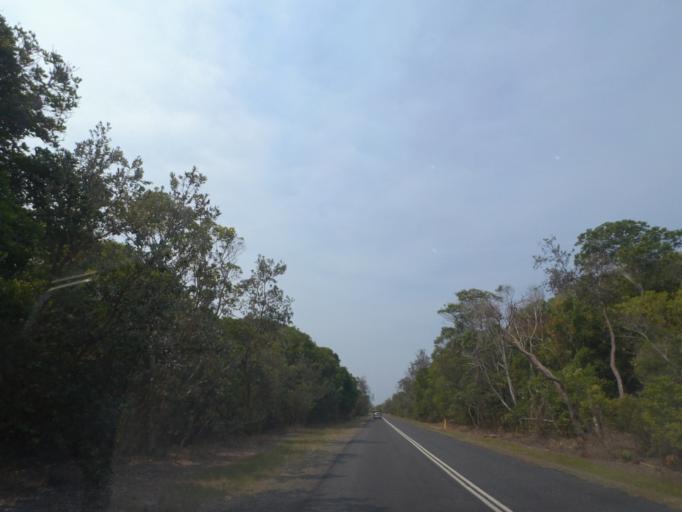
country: AU
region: New South Wales
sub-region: Tweed
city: Pottsville Beach
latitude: -28.4366
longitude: 153.5559
